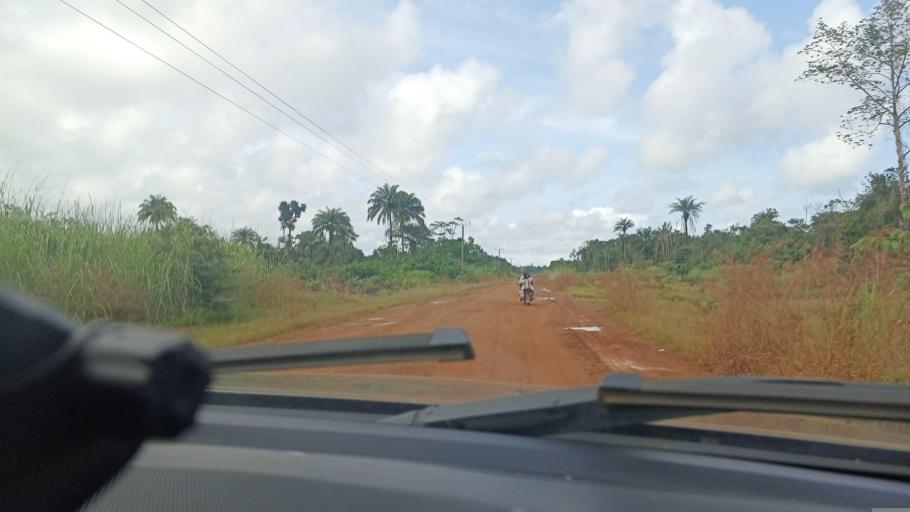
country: LR
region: Grand Cape Mount
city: Robertsport
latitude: 6.6834
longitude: -11.1282
